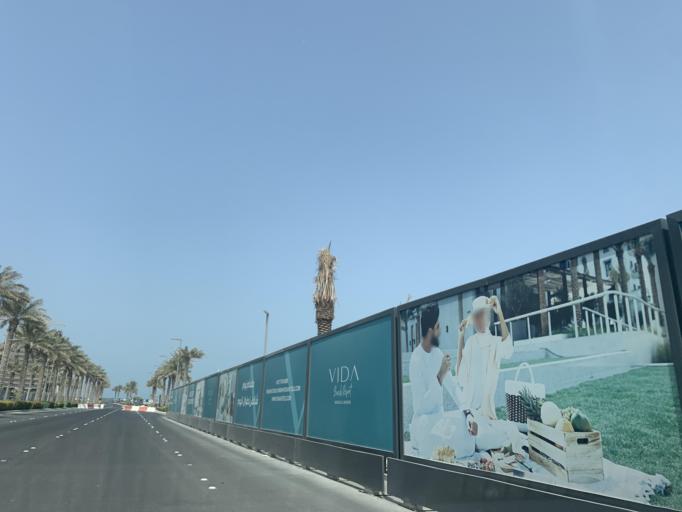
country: BH
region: Muharraq
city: Al Muharraq
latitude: 26.3059
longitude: 50.6429
